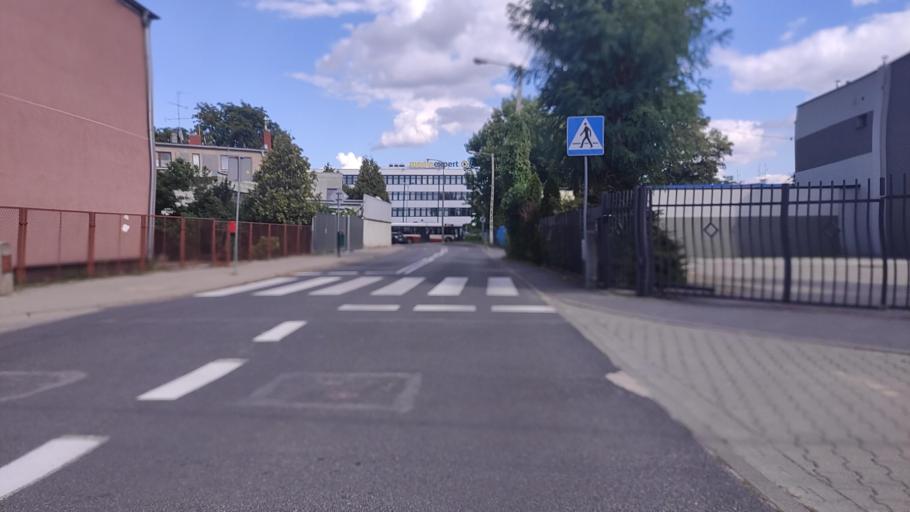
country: PL
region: Greater Poland Voivodeship
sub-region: Powiat poznanski
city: Swarzedz
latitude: 52.4053
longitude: 17.0723
